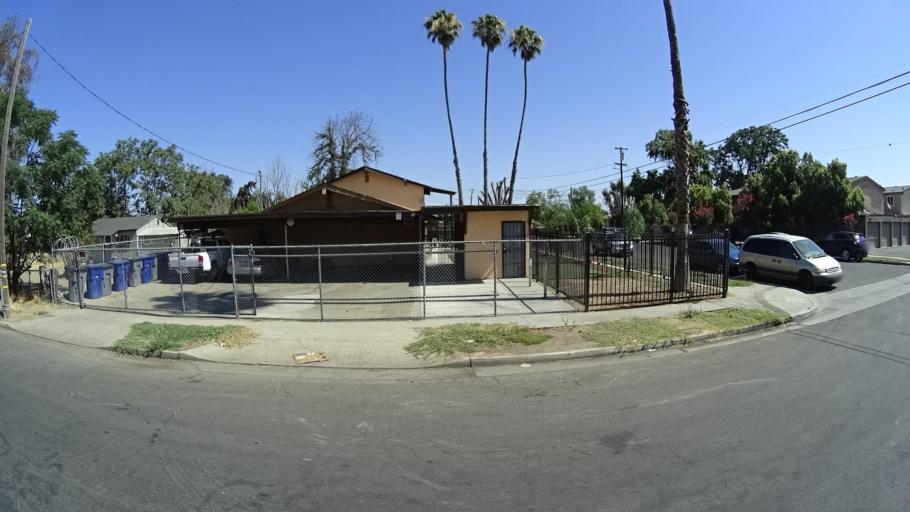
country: US
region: California
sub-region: Fresno County
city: Fresno
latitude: 36.7595
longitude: -119.7524
